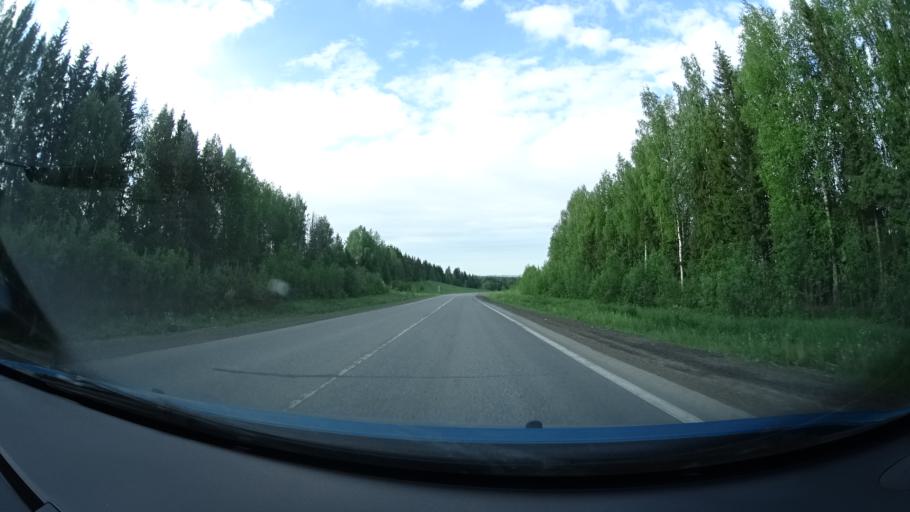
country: RU
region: Perm
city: Osa
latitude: 57.4017
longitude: 55.6235
